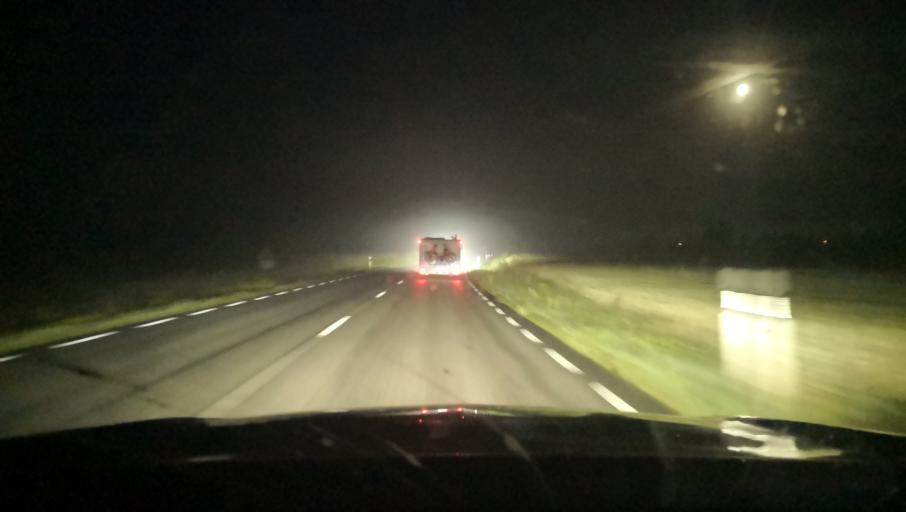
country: SE
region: Skane
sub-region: Kristianstads Kommun
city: Degeberga
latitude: 55.8495
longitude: 14.0958
